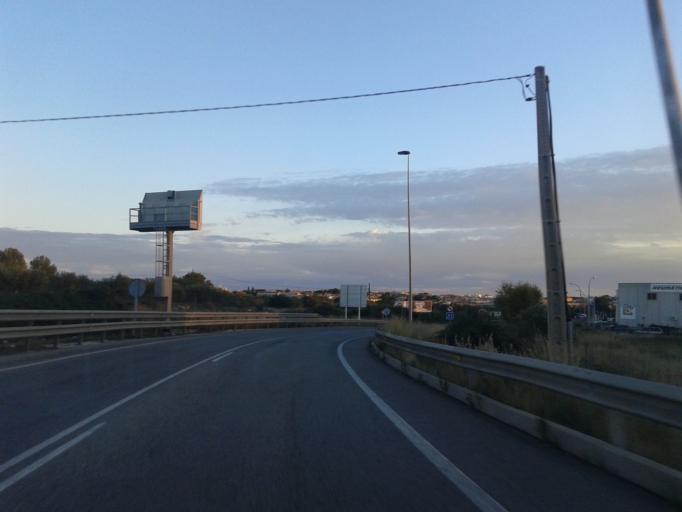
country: ES
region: Catalonia
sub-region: Provincia de Tarragona
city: Torredembarra
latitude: 41.1580
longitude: 1.3923
